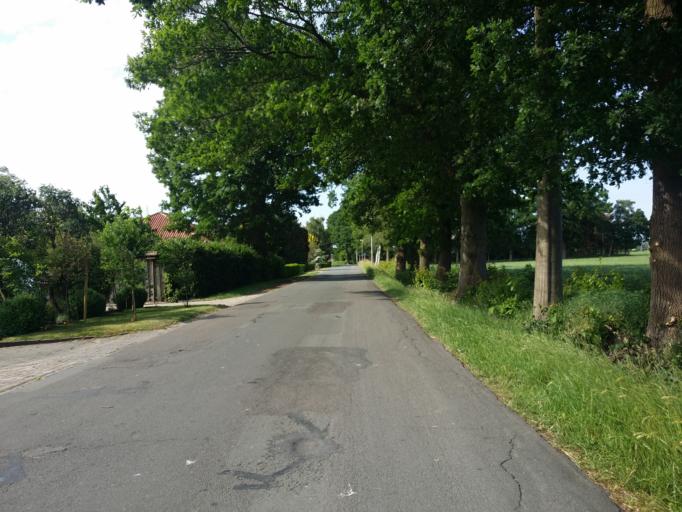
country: DE
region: Lower Saxony
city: Bockhorn
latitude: 53.3381
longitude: 8.0312
